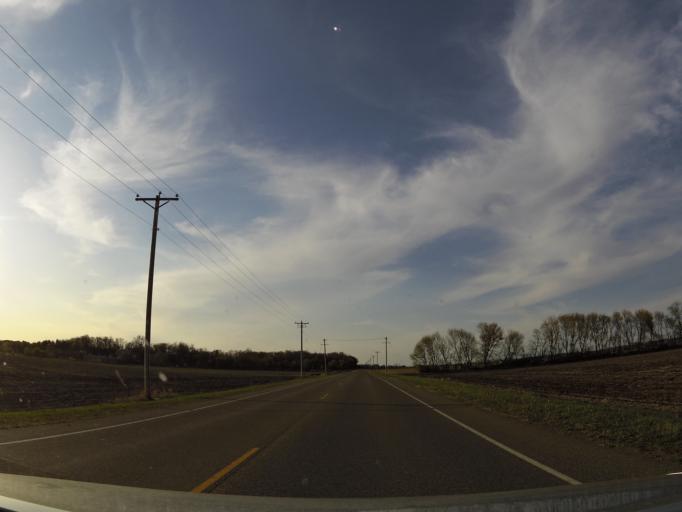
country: US
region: Wisconsin
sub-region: Pierce County
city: River Falls
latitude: 44.9010
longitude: -92.6744
